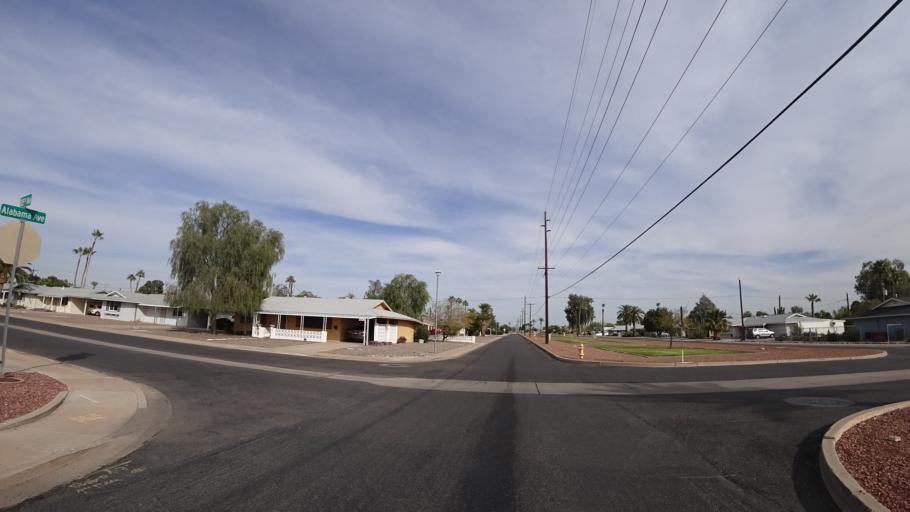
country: US
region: Arizona
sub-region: Maricopa County
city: Sun City
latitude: 33.5949
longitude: -112.2856
